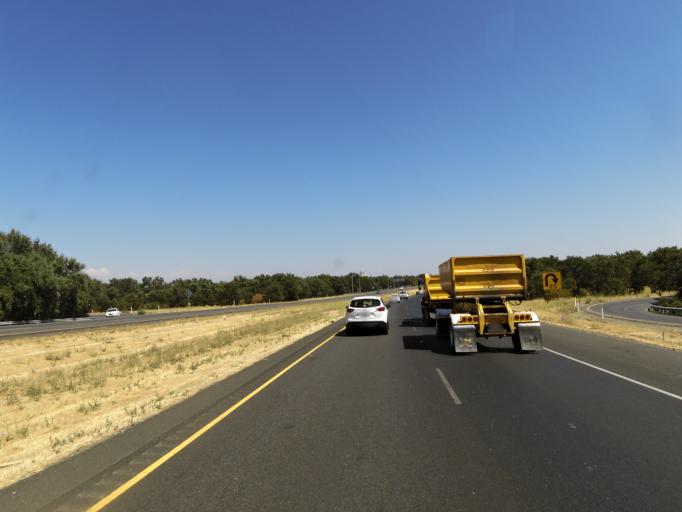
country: US
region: California
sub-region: Yolo County
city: Woodland
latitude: 38.6959
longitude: -121.7634
